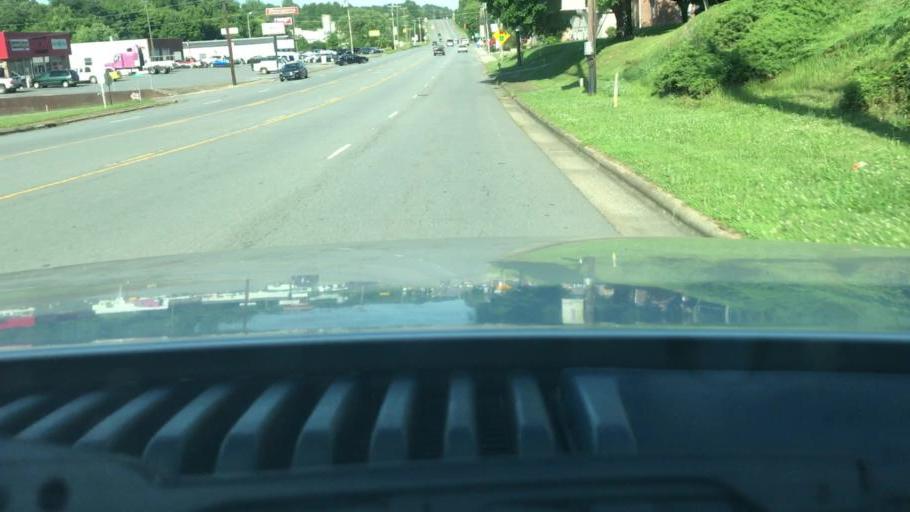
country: US
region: North Carolina
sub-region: Yadkin County
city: Jonesville
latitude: 36.2403
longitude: -80.8347
